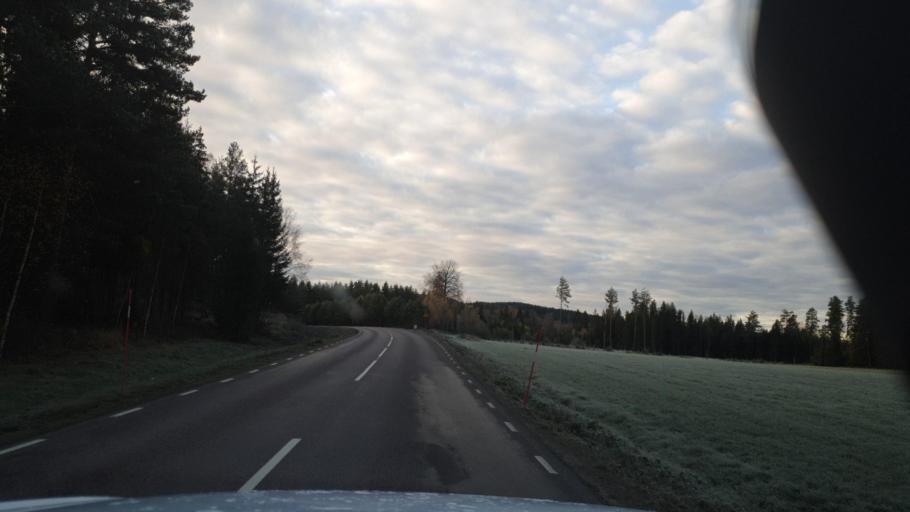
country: SE
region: Vaermland
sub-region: Eda Kommun
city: Amotfors
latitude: 59.7332
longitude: 12.1701
